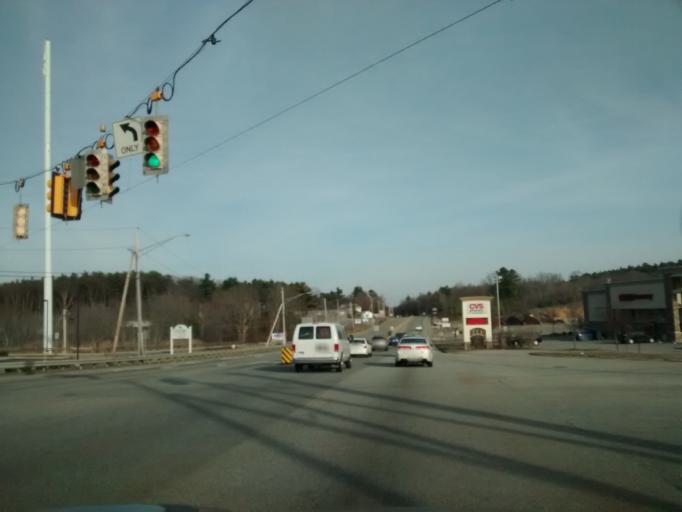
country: US
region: Massachusetts
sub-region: Worcester County
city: Charlton
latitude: 42.1457
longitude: -71.9696
